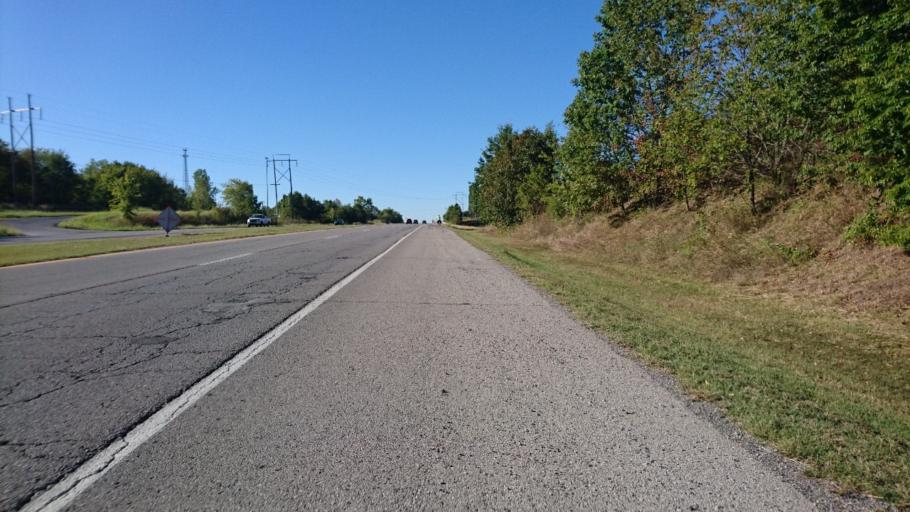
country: US
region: Oklahoma
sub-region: Rogers County
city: Catoosa
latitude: 36.2054
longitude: -95.7265
